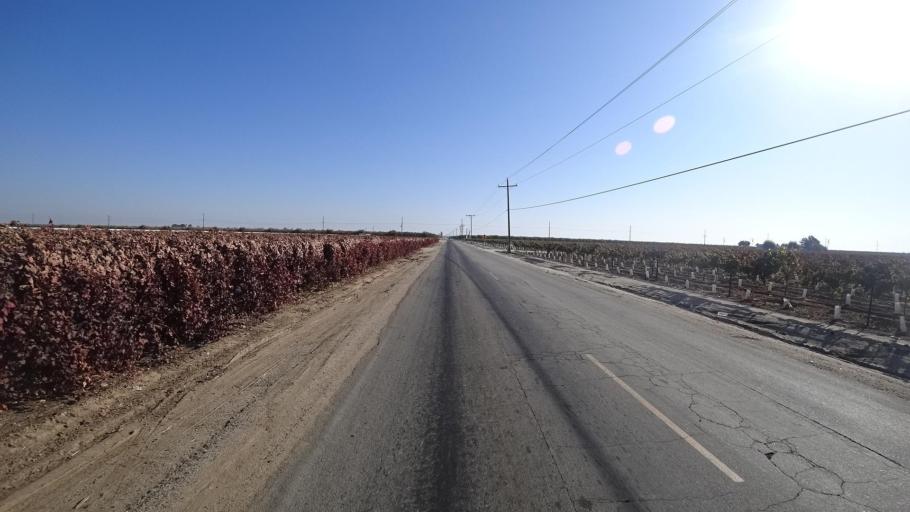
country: US
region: California
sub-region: Kern County
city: McFarland
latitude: 35.7177
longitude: -119.2080
